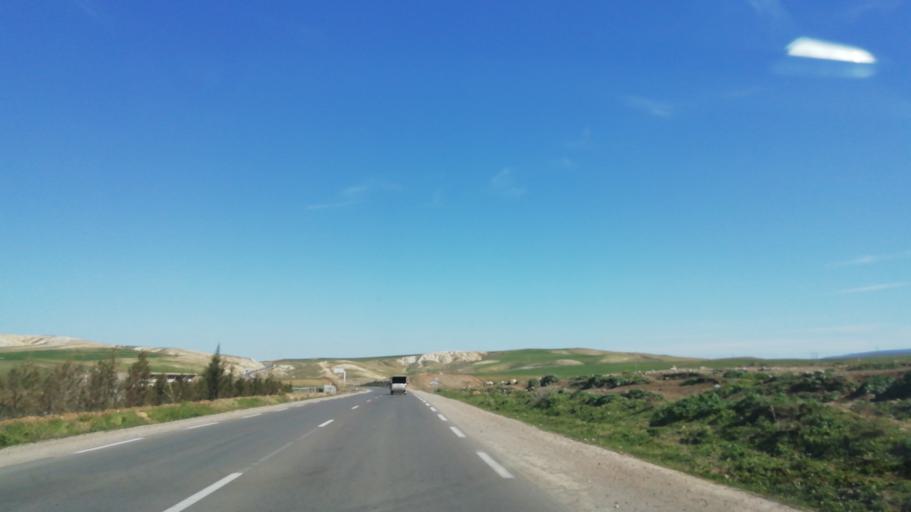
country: DZ
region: Mascara
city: Oued el Abtal
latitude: 35.4486
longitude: 0.6159
